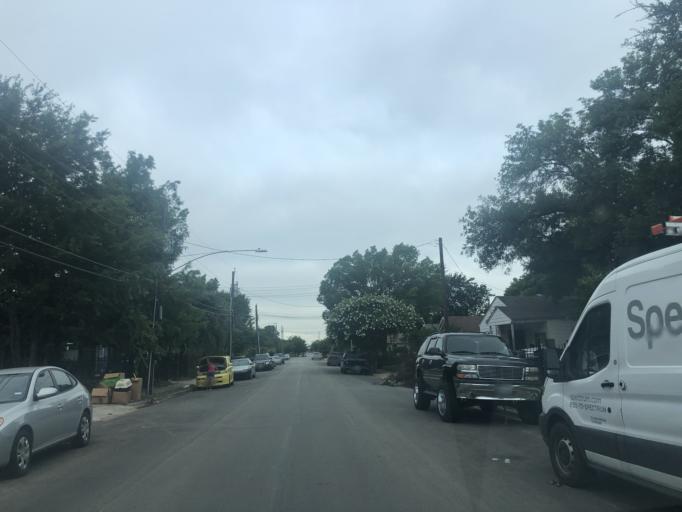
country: US
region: Texas
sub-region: Dallas County
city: Dallas
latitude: 32.7870
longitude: -96.8450
